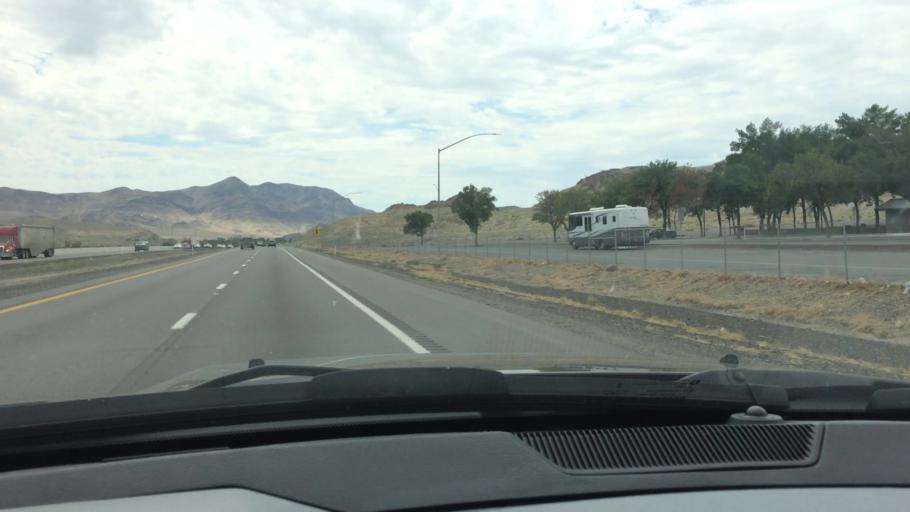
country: US
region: Nevada
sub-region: Lyon County
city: Fernley
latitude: 39.6028
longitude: -119.3356
